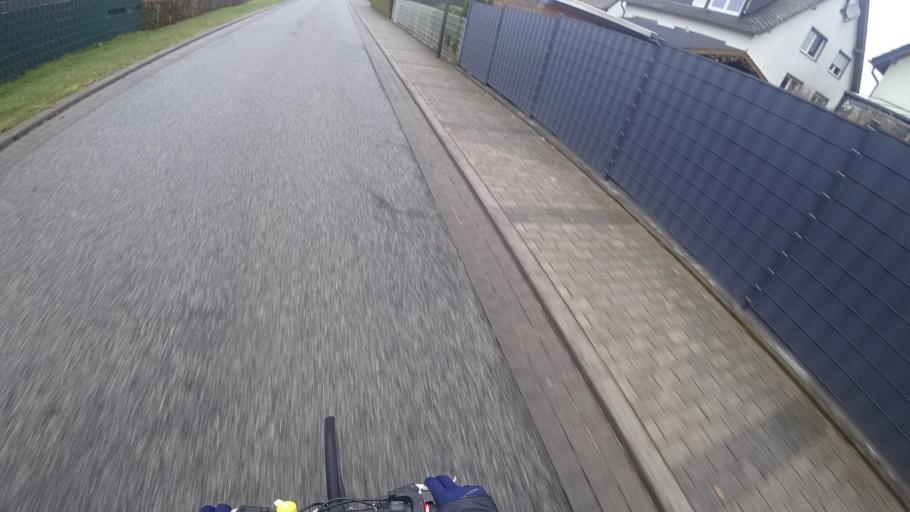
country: DE
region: Rheinland-Pfalz
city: Halsenbach
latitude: 50.1709
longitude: 7.5566
